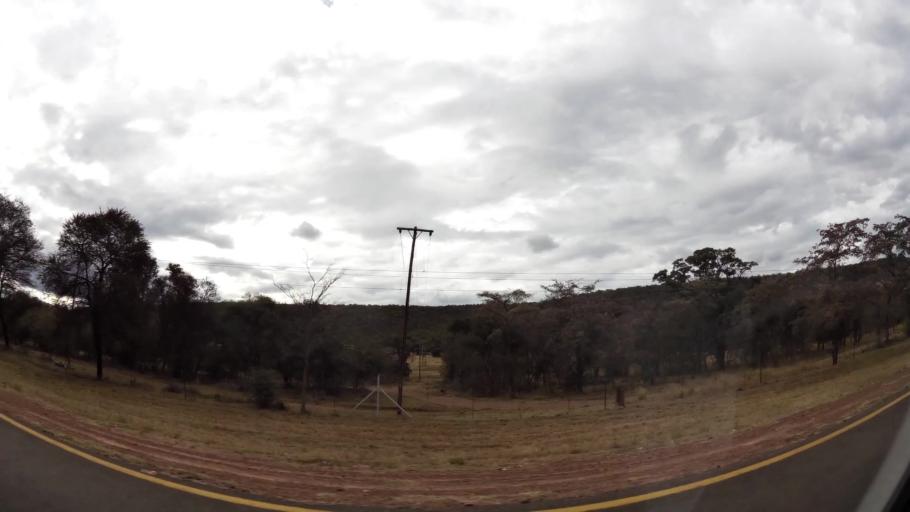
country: ZA
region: Limpopo
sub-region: Waterberg District Municipality
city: Modimolle
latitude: -24.6663
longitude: 28.4624
